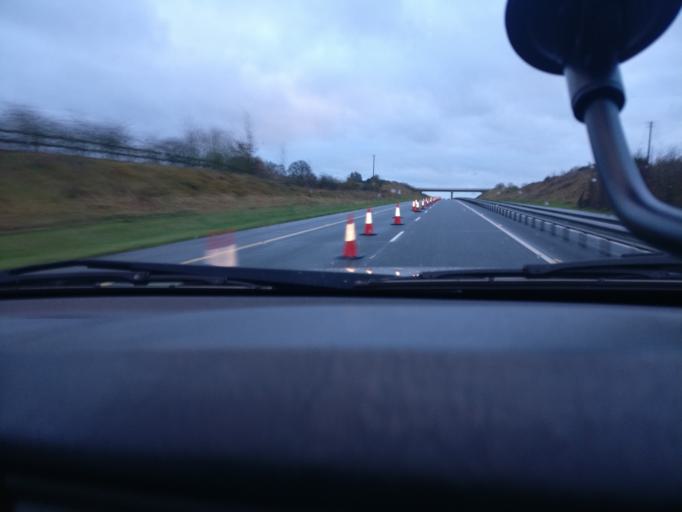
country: IE
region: Leinster
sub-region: An Iarmhi
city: Athlone
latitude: 53.3864
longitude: -8.0504
